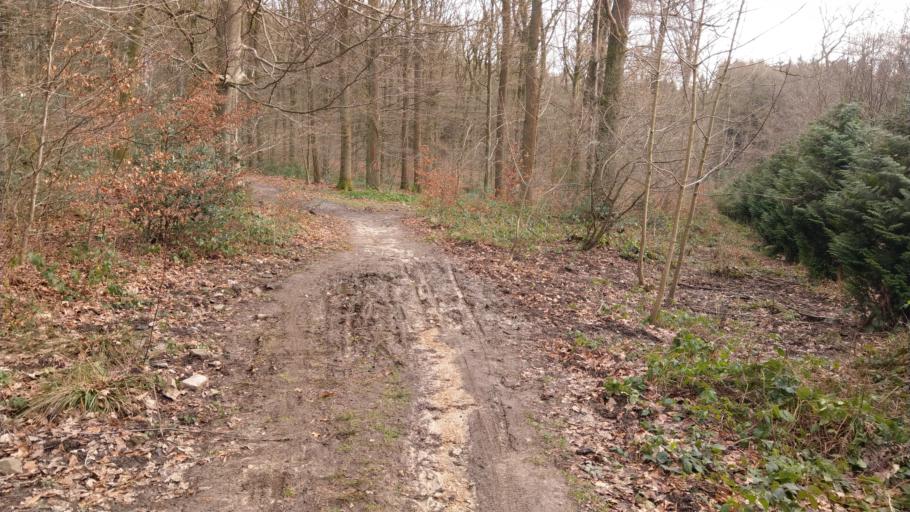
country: BE
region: Wallonia
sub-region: Province de Liege
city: La Calamine
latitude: 50.7401
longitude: 6.0307
